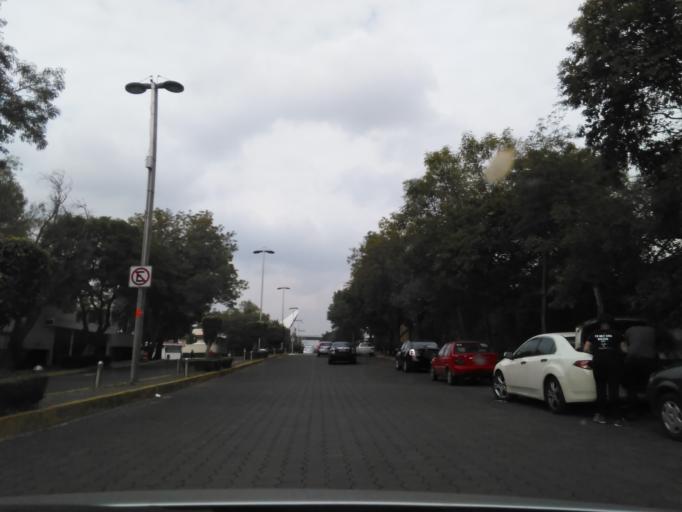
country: MX
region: Mexico City
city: Tlalpan
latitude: 19.2970
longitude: -99.1923
